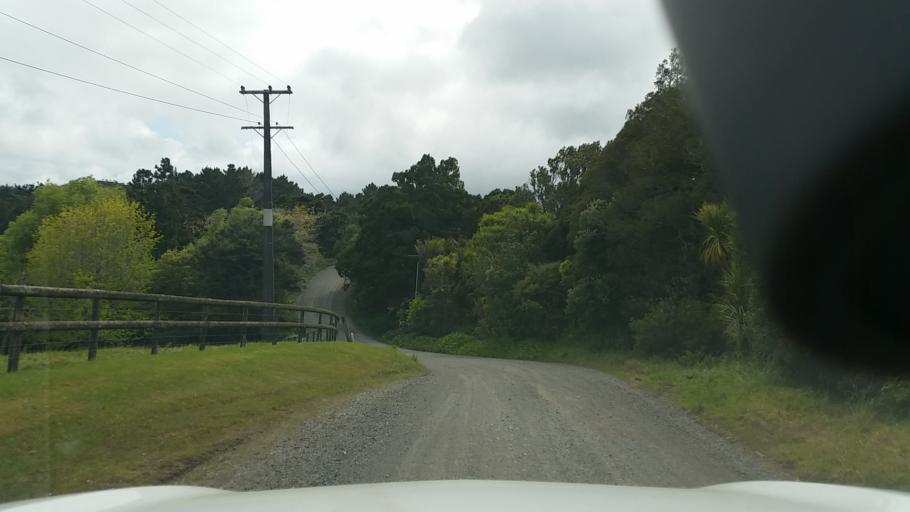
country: NZ
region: Auckland
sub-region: Auckland
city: Muriwai Beach
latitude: -36.8451
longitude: 174.5107
